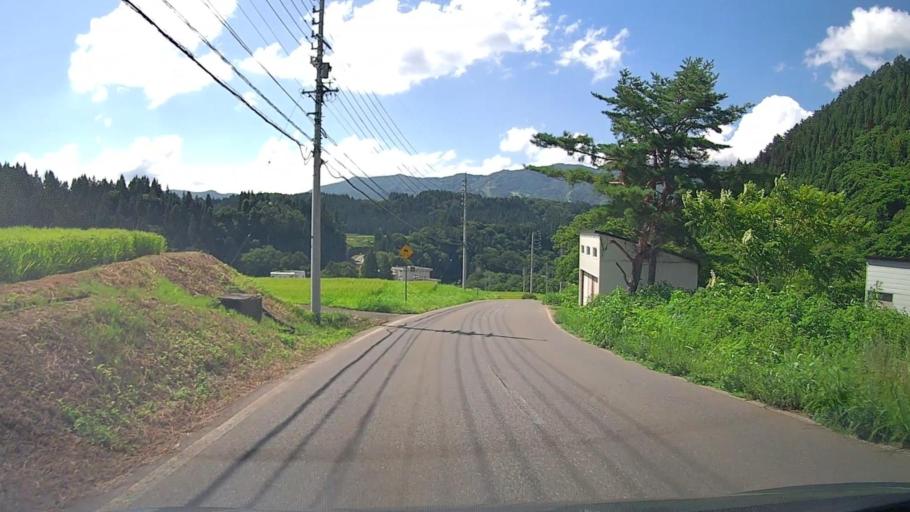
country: JP
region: Nagano
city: Iiyama
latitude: 36.9231
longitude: 138.4304
